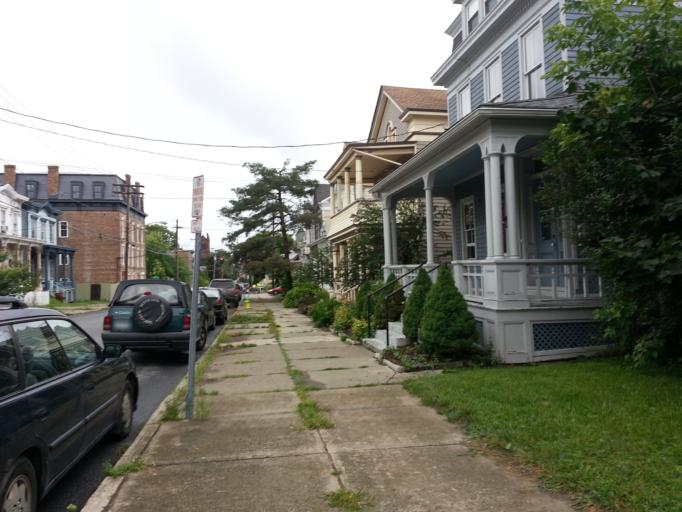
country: US
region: New York
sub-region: Columbia County
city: Hudson
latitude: 42.2485
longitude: -73.7866
